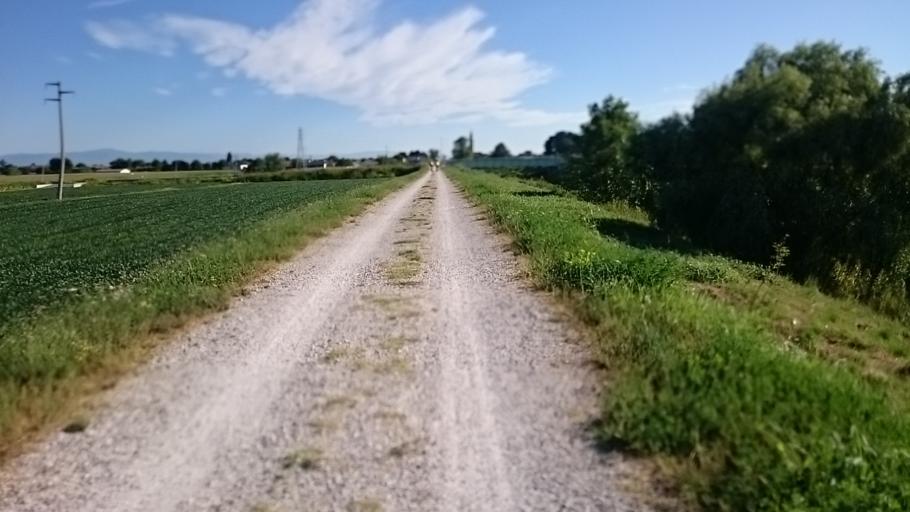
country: IT
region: Veneto
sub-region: Provincia di Padova
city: Campodarsego
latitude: 45.4931
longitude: 11.9032
